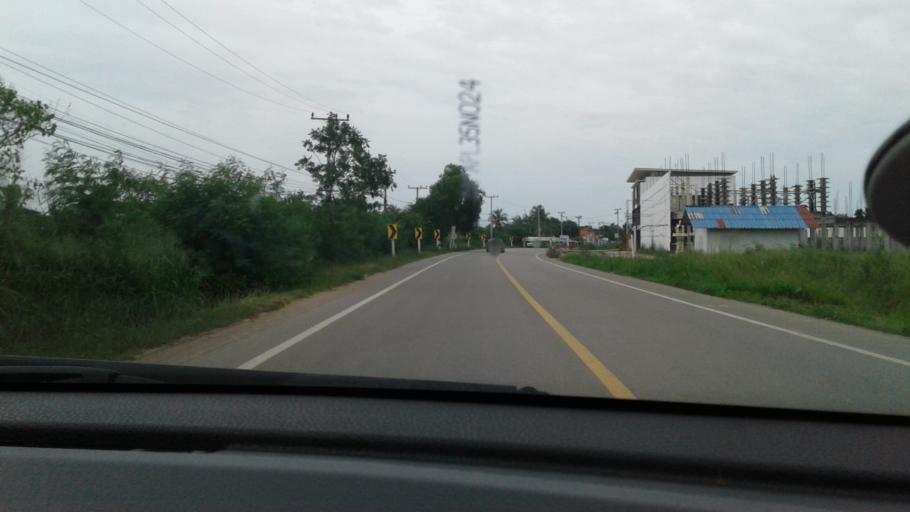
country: TH
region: Prachuap Khiri Khan
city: Pran Buri
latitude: 12.3872
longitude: 99.9847
